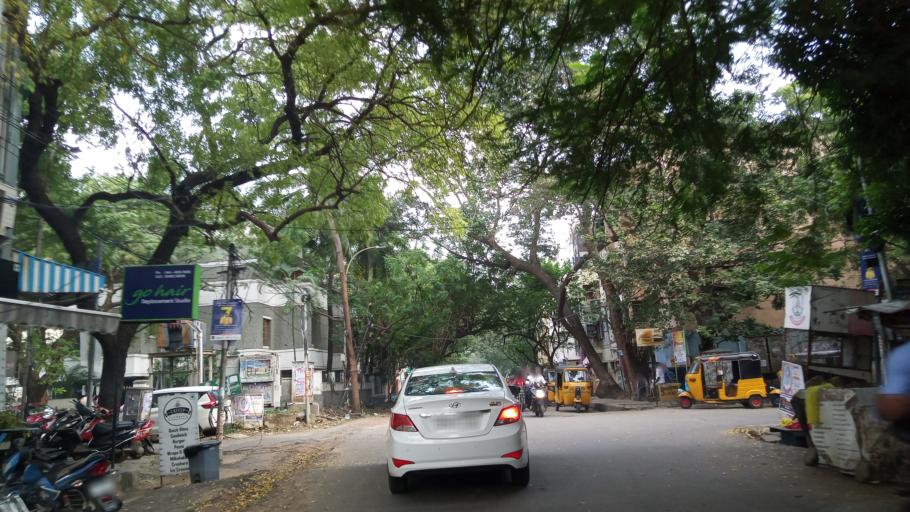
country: IN
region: Tamil Nadu
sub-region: Kancheepuram
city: Alandur
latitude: 13.0373
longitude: 80.2142
